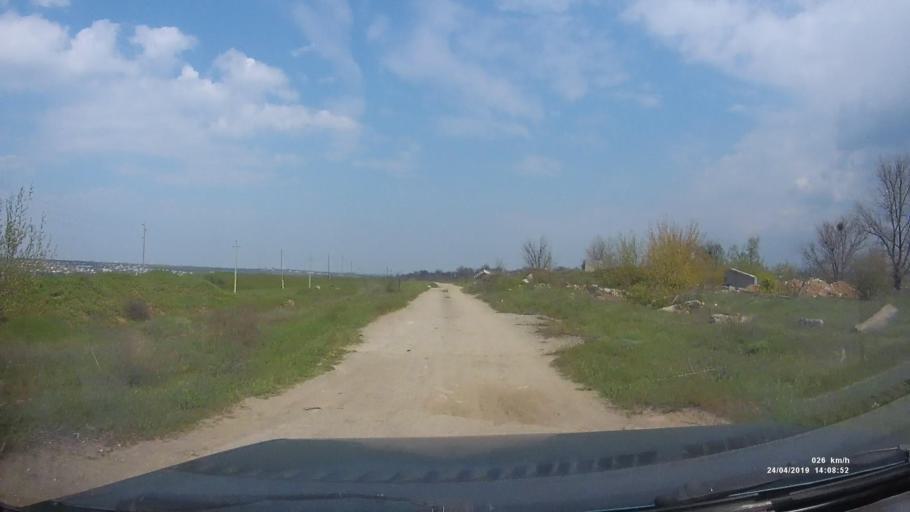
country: RU
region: Kalmykiya
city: Arshan'
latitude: 46.2636
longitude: 44.2198
